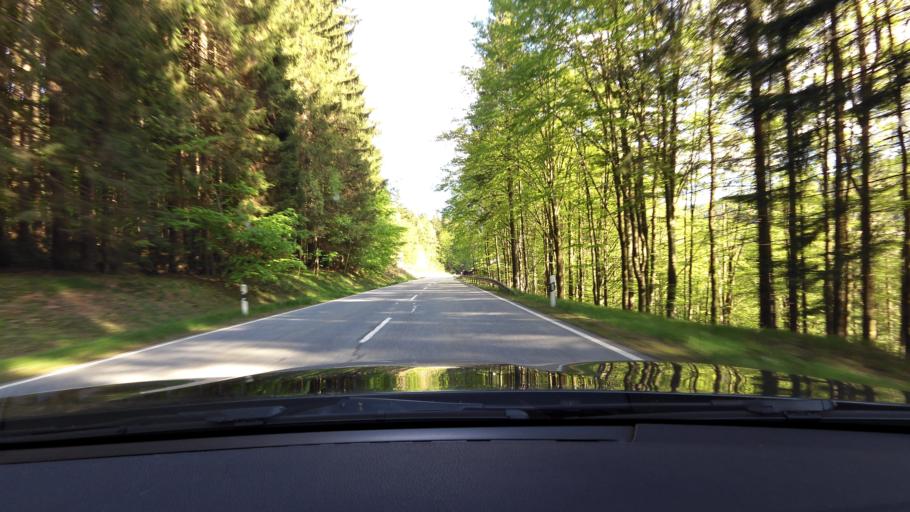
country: DE
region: Bavaria
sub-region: Lower Bavaria
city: Bayerisch Eisenstein
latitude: 49.0812
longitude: 13.2080
